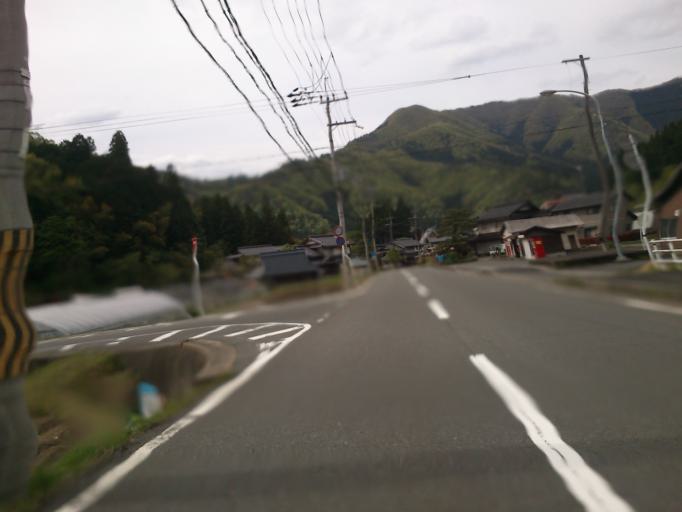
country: JP
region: Kyoto
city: Ayabe
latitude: 35.2614
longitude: 135.4441
